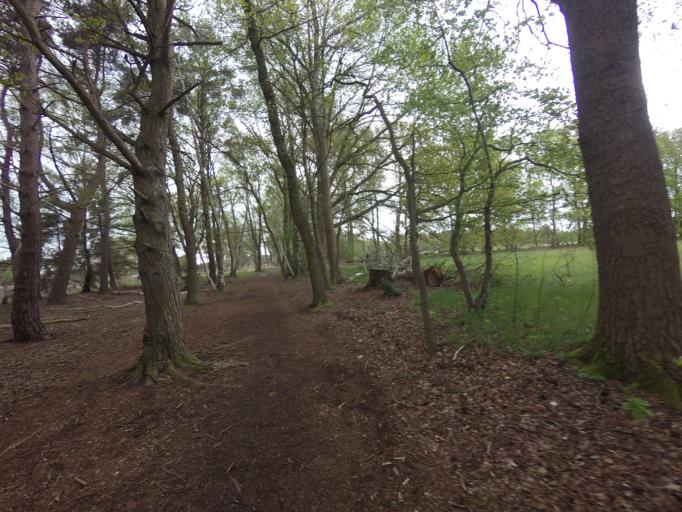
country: NL
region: Overijssel
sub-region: Gemeente Haaksbergen
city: Haaksbergen
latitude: 52.1549
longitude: 6.8059
